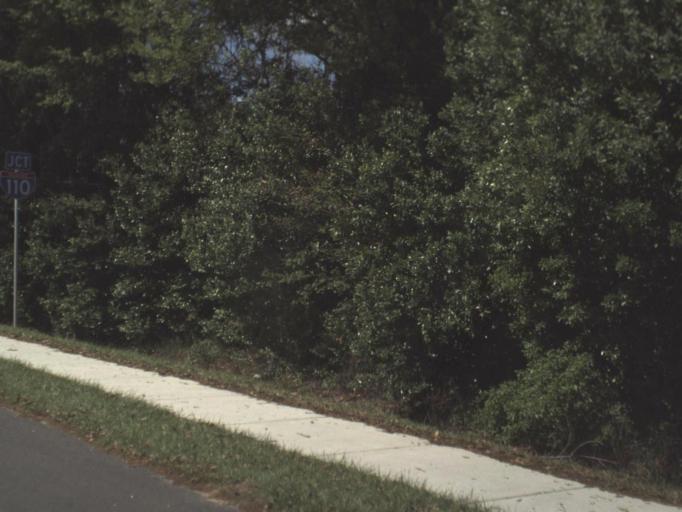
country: US
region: Florida
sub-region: Escambia County
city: Goulding
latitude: 30.4508
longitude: -87.2171
